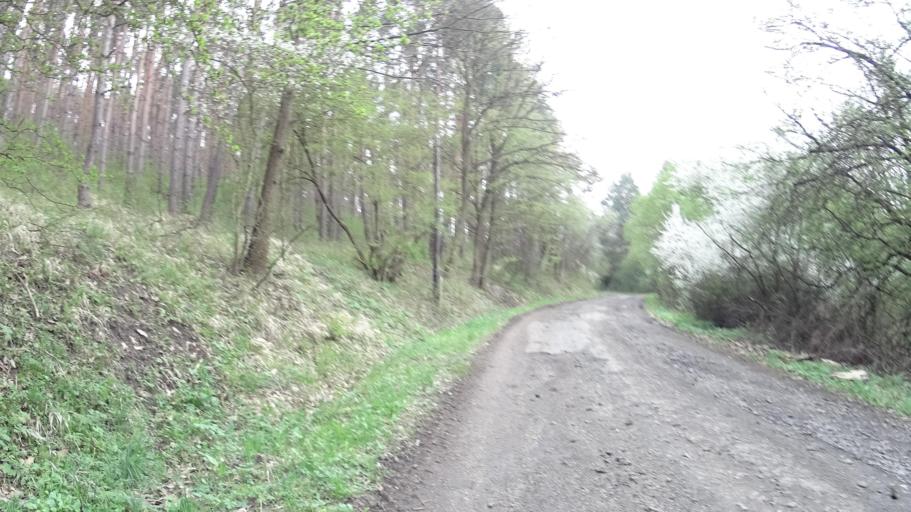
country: HU
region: Pest
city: Kismaros
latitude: 47.8691
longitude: 19.0270
